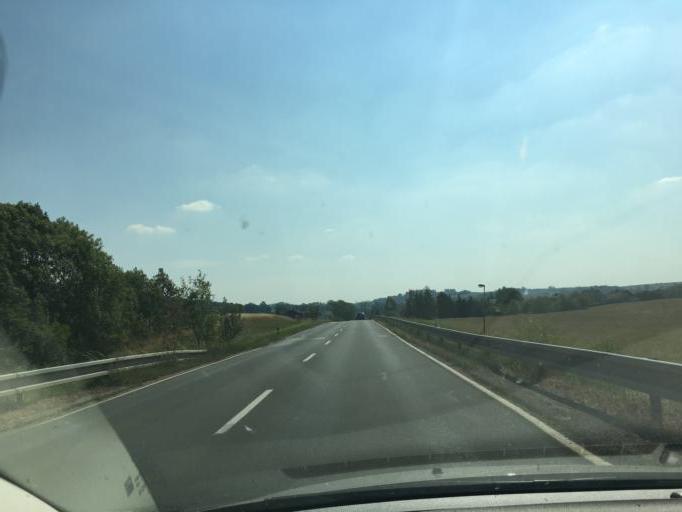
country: CZ
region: Kralovehradecky
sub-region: Okres Trutnov
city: Vrchlabi
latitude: 50.6218
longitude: 15.6486
